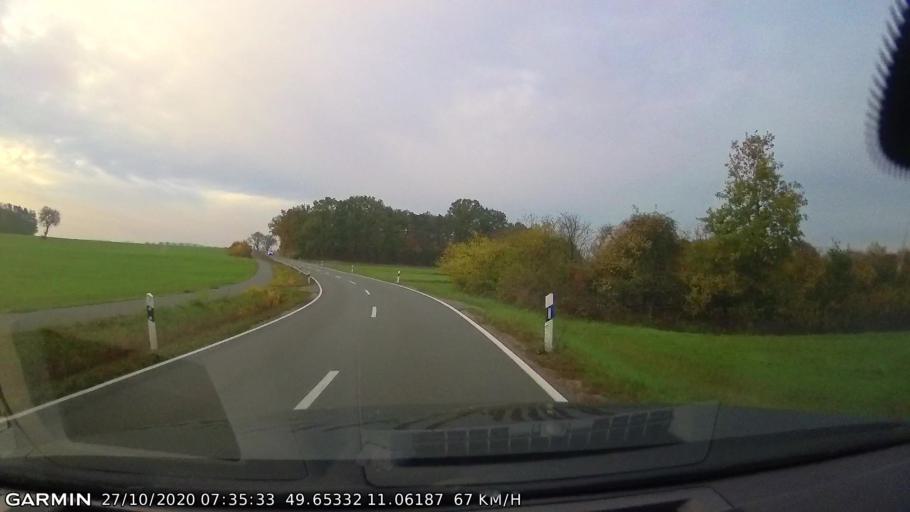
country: DE
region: Bavaria
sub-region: Upper Franconia
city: Poxdorf
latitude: 49.6531
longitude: 11.0620
